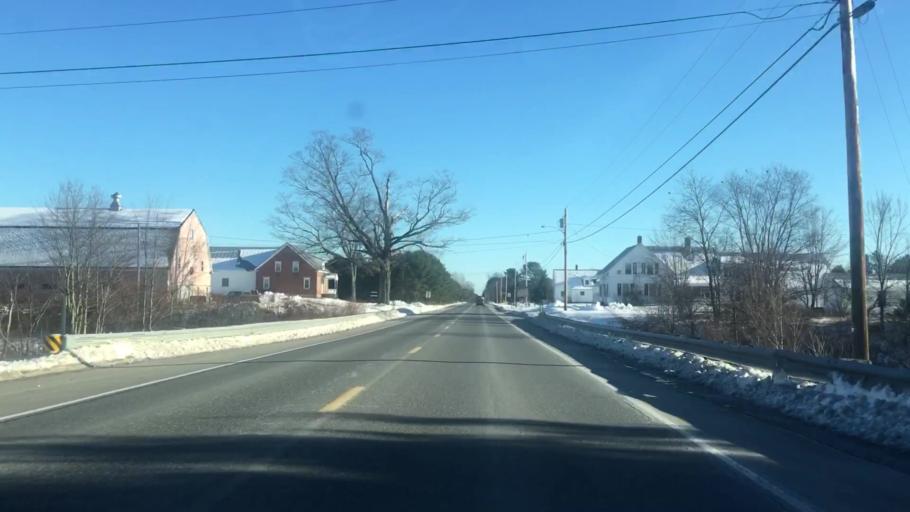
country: US
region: Maine
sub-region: Somerset County
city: Norridgewock
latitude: 44.7082
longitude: -69.7760
